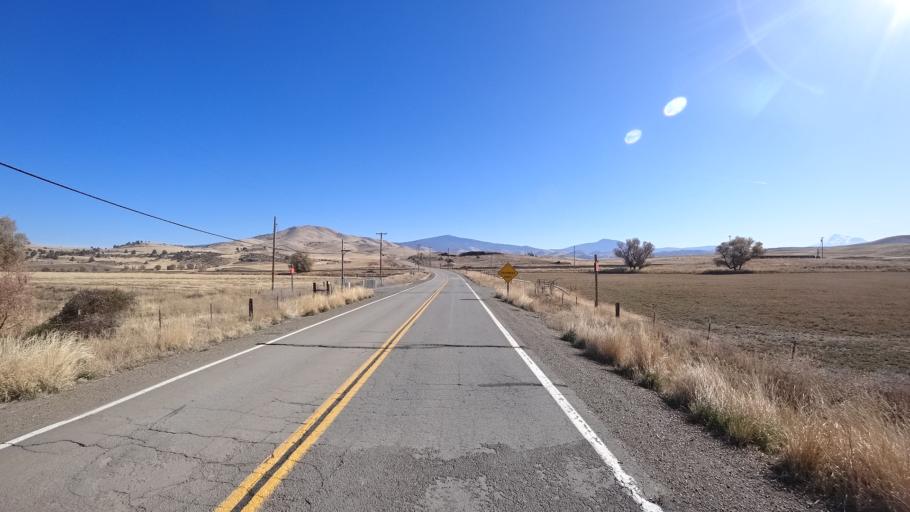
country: US
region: California
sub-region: Siskiyou County
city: Montague
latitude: 41.8481
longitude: -122.4674
